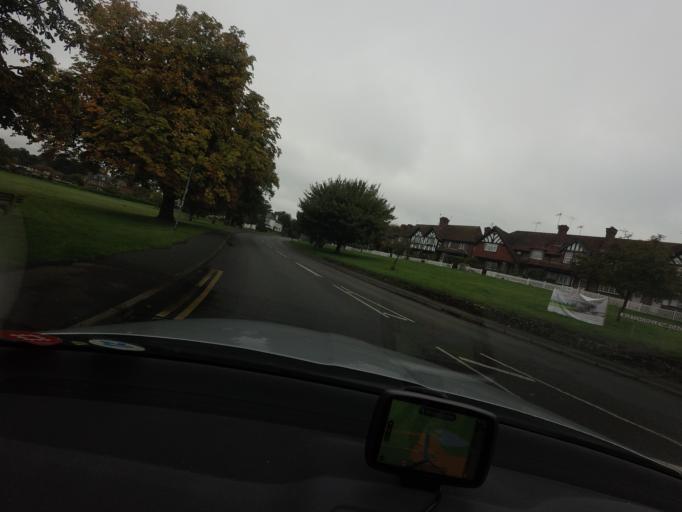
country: GB
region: England
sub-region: Surrey
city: Godstone
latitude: 51.2481
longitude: -0.0682
